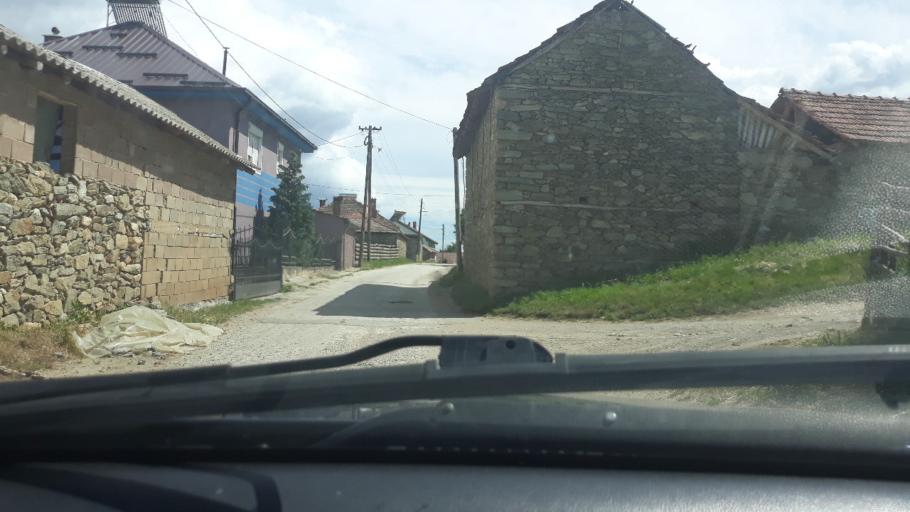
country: MK
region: Krivogastani
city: Krivogashtani
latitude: 41.3238
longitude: 21.3043
